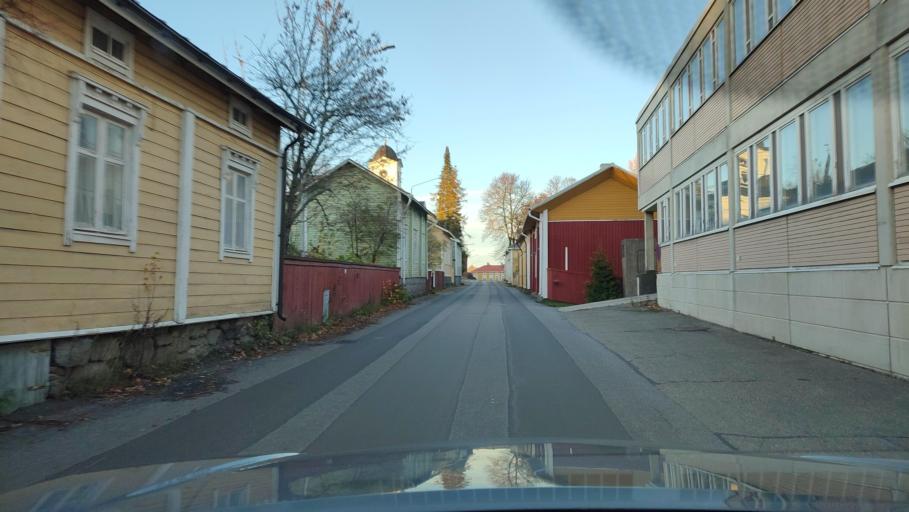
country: FI
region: Ostrobothnia
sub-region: Sydosterbotten
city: Kristinestad
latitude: 62.2731
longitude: 21.3734
